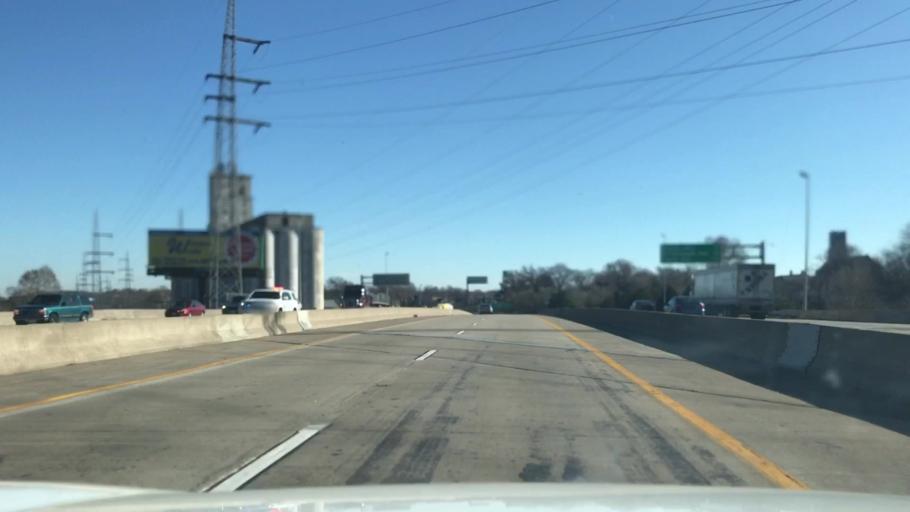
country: US
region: Missouri
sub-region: Saint Louis County
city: Pine Lawn
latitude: 38.6847
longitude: -90.2427
